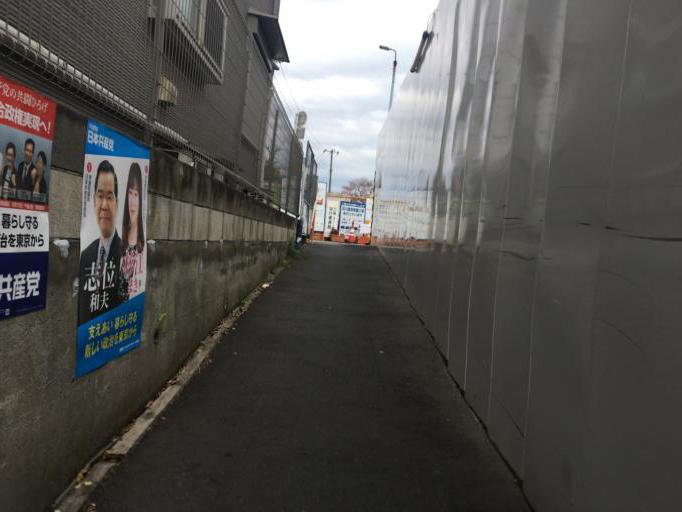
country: JP
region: Tokyo
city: Tokyo
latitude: 35.7185
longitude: 139.6396
